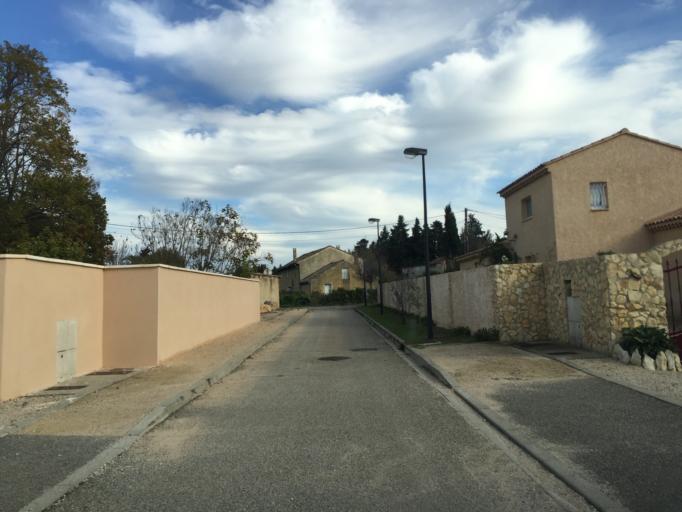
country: FR
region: Provence-Alpes-Cote d'Azur
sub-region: Departement du Vaucluse
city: Orange
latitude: 44.1142
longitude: 4.8011
